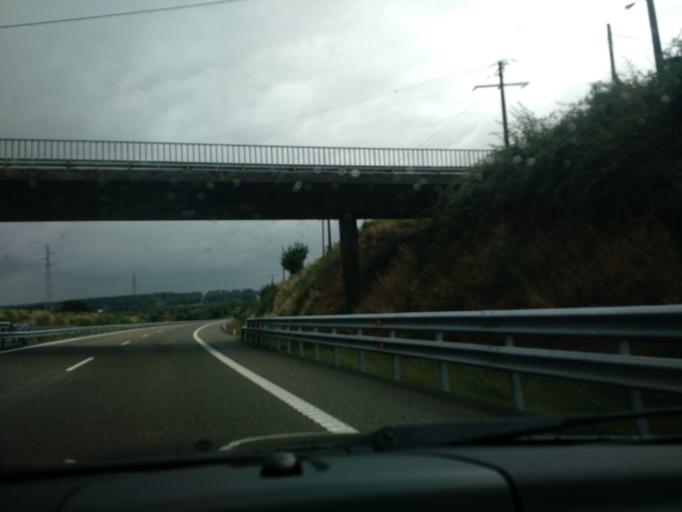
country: ES
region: Galicia
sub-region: Provincia da Coruna
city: Oroso
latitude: 42.9614
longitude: -8.4563
